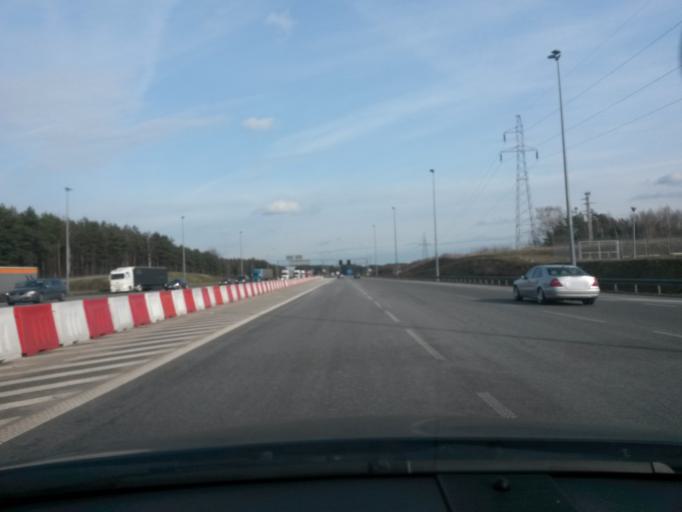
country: PL
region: Greater Poland Voivodeship
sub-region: Powiat koninski
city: Stare Miasto
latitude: 52.1520
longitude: 18.2790
